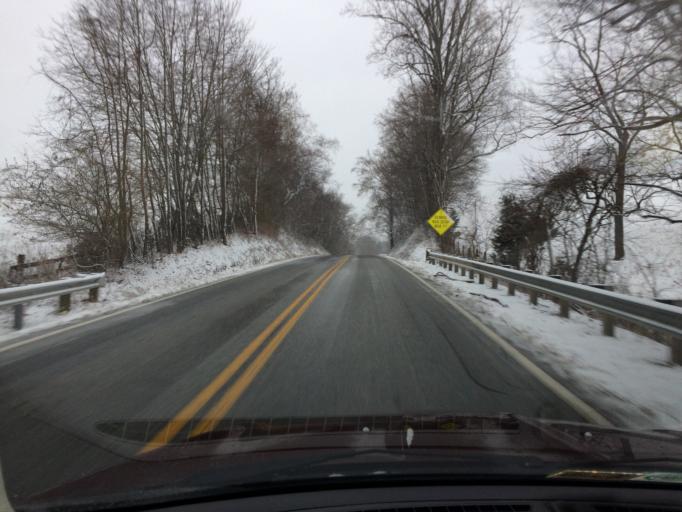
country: US
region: Virginia
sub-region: Amherst County
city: Amherst
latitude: 37.6530
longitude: -79.1363
